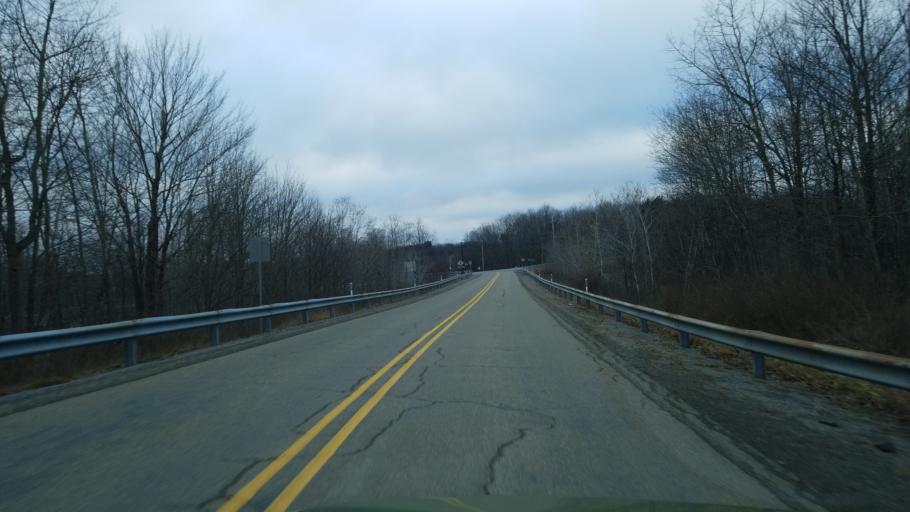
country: US
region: Pennsylvania
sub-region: Jefferson County
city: Falls Creek
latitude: 41.1589
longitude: -78.8225
